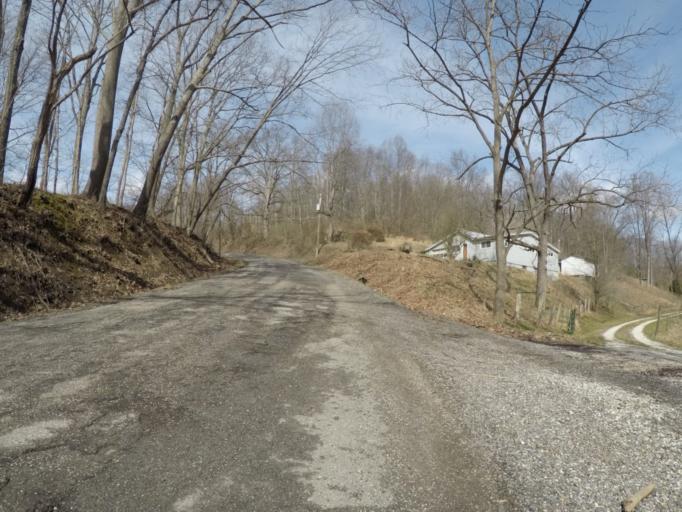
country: US
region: Ohio
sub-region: Lawrence County
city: Burlington
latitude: 38.4839
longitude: -82.5346
